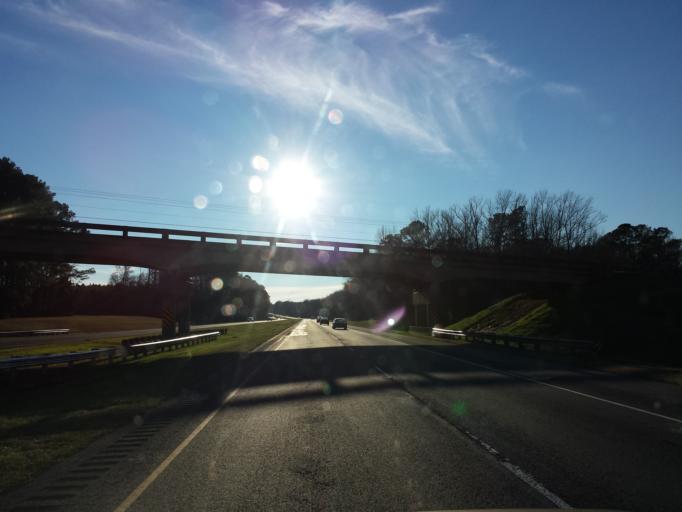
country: US
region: Alabama
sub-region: Greene County
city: Eutaw
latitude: 32.8691
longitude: -87.9240
